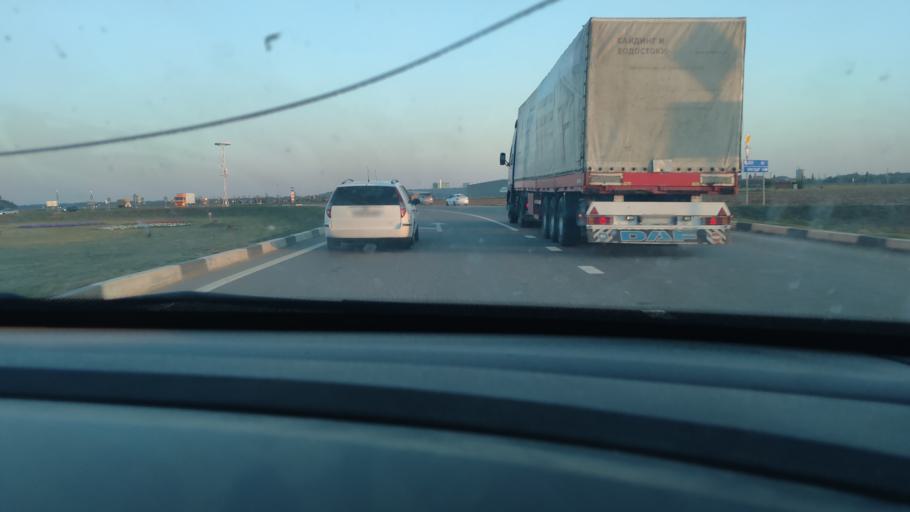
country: RU
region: Krasnodarskiy
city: Timashevsk
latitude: 45.6389
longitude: 38.9705
